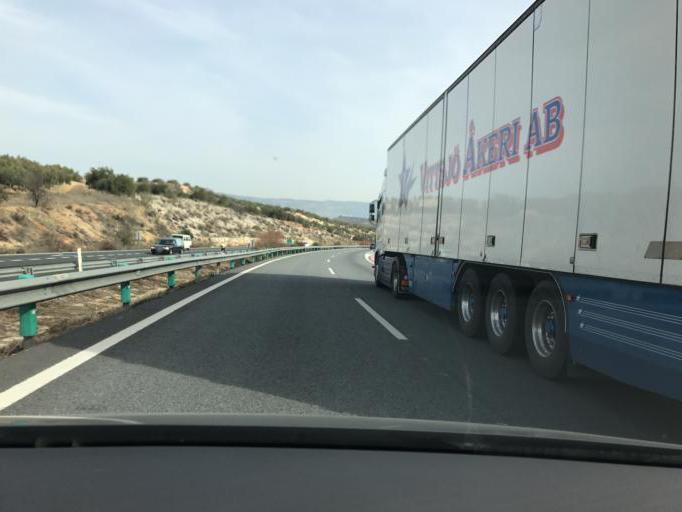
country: ES
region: Andalusia
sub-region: Provincia de Granada
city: Loja
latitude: 37.1546
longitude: -4.2245
